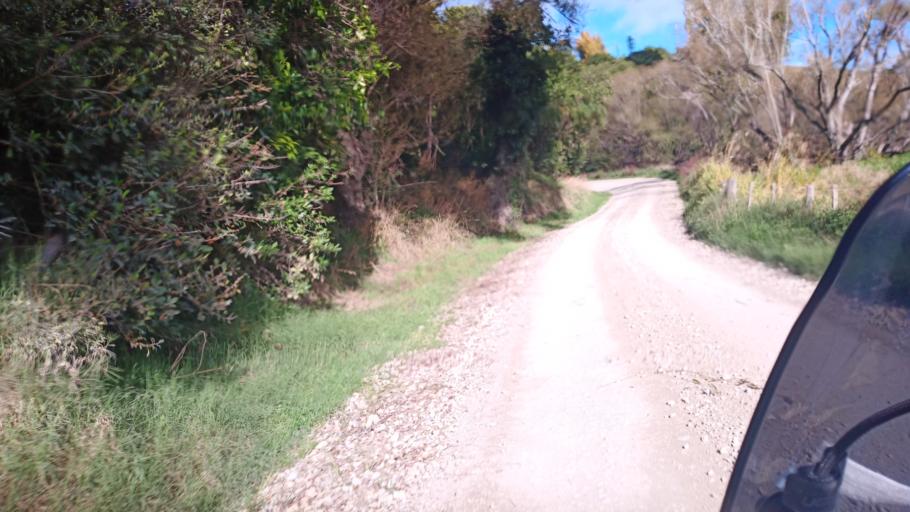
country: NZ
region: Gisborne
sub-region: Gisborne District
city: Gisborne
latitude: -38.5382
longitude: 177.5196
